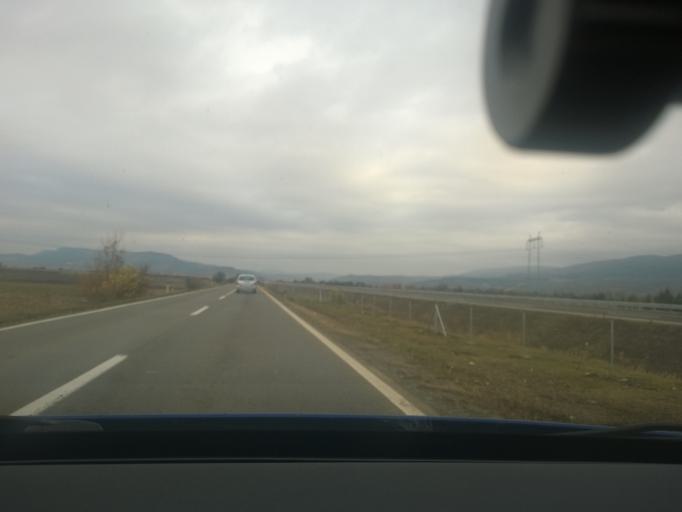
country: RS
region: Central Serbia
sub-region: Pirotski Okrug
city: Pirot
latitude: 43.1123
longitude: 22.6302
